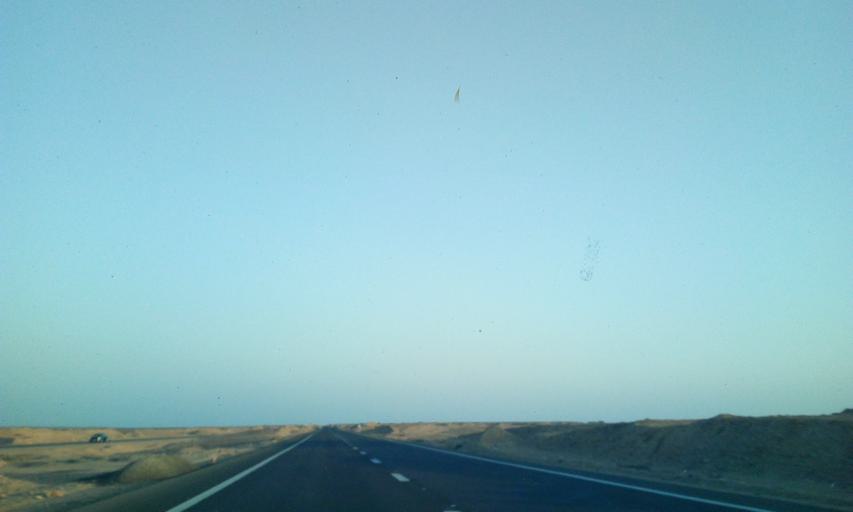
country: EG
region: Red Sea
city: El Gouna
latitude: 27.7722
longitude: 33.4864
